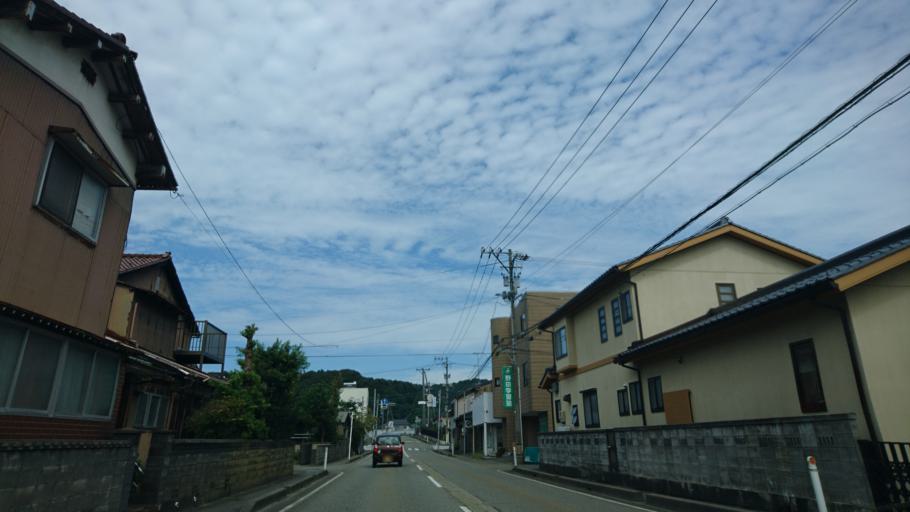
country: JP
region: Ishikawa
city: Komatsu
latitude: 36.3101
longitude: 136.3168
